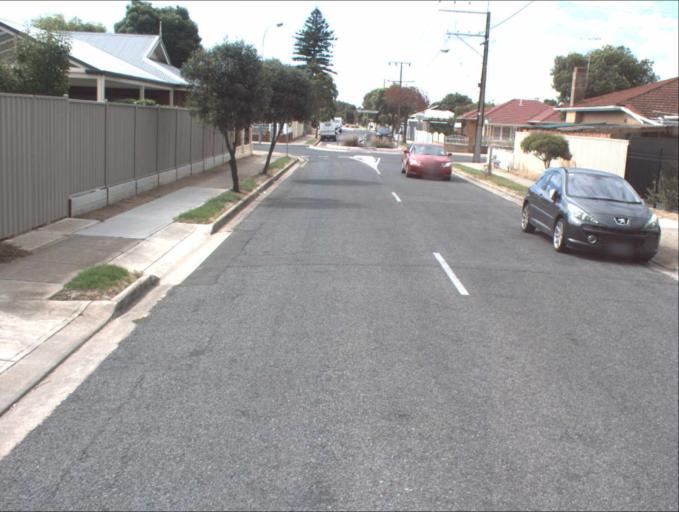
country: AU
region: South Australia
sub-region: Port Adelaide Enfield
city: Blair Athol
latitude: -34.8624
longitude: 138.5895
